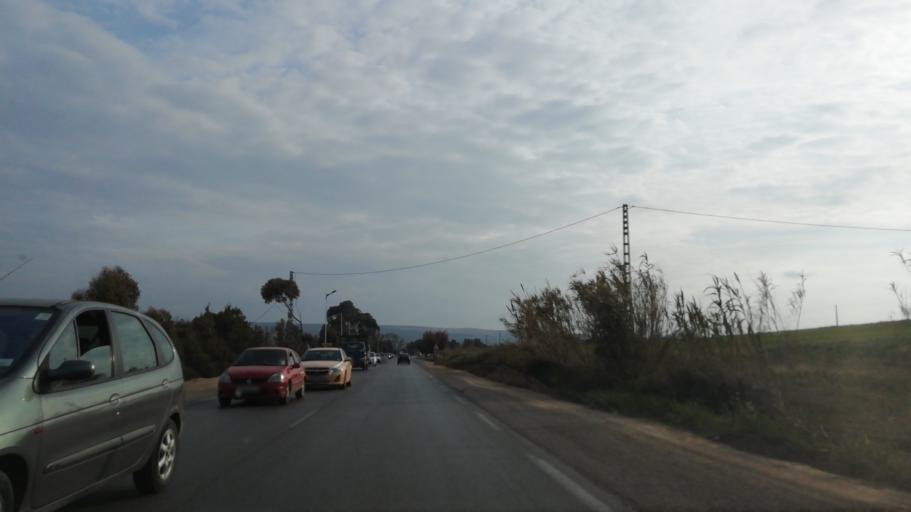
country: DZ
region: Mostaganem
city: Mostaganem
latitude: 35.8820
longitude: 0.0782
